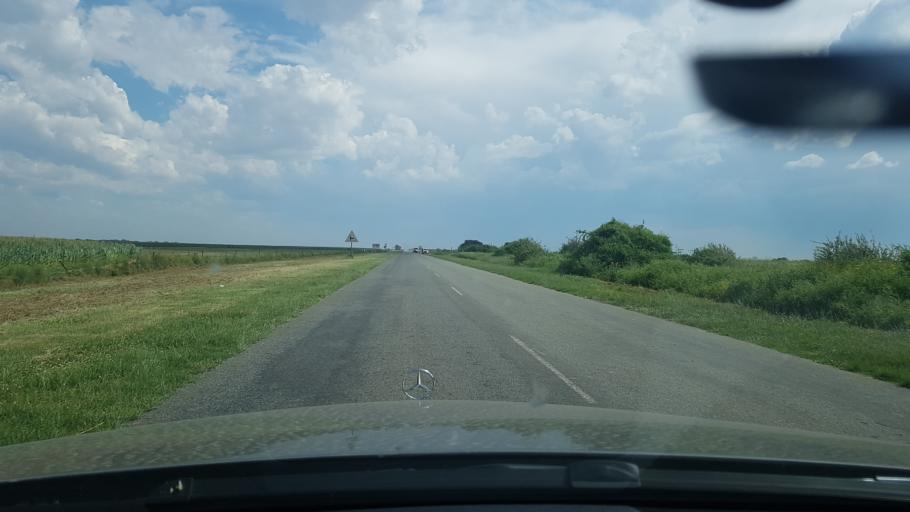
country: ZA
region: North-West
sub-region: Dr Ruth Segomotsi Mompati District Municipality
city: Bloemhof
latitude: -27.6709
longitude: 25.5909
